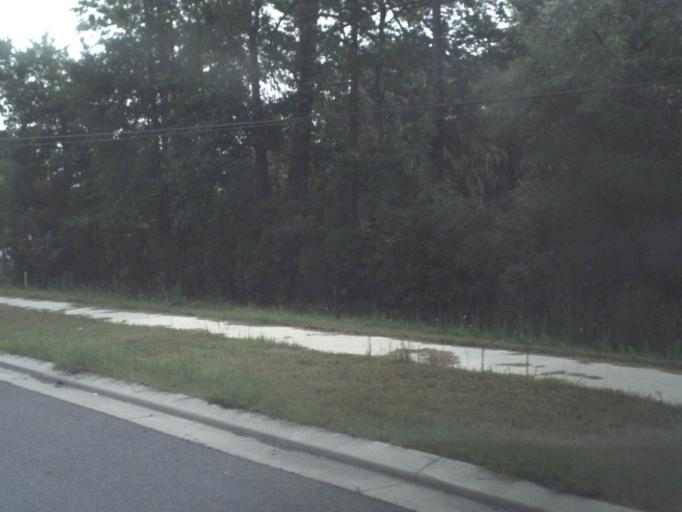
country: US
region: Florida
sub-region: Duval County
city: Baldwin
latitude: 30.3824
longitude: -81.9395
